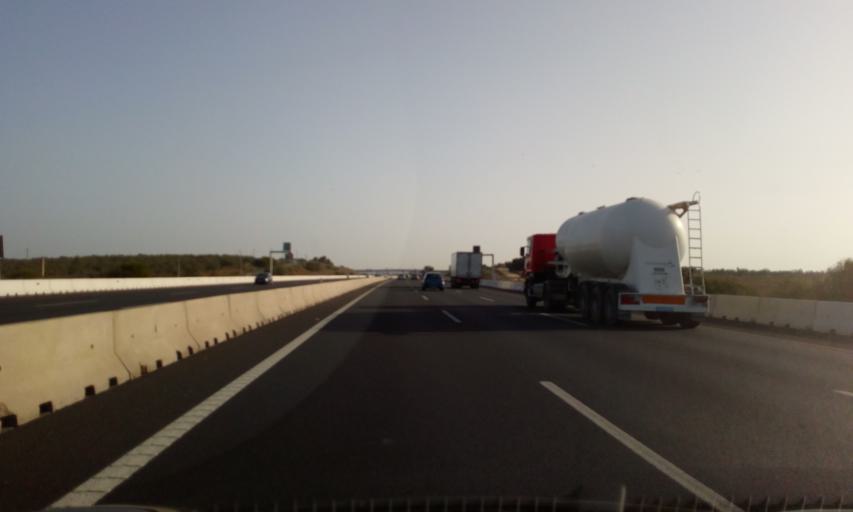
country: ES
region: Andalusia
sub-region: Provincia de Sevilla
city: Espartinas
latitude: 37.3635
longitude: -6.1272
